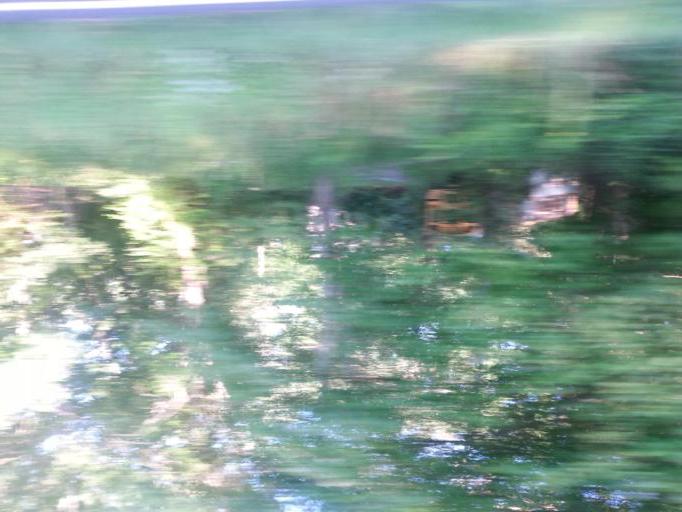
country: US
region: Tennessee
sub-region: Blount County
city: Maryville
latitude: 35.6543
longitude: -83.9055
